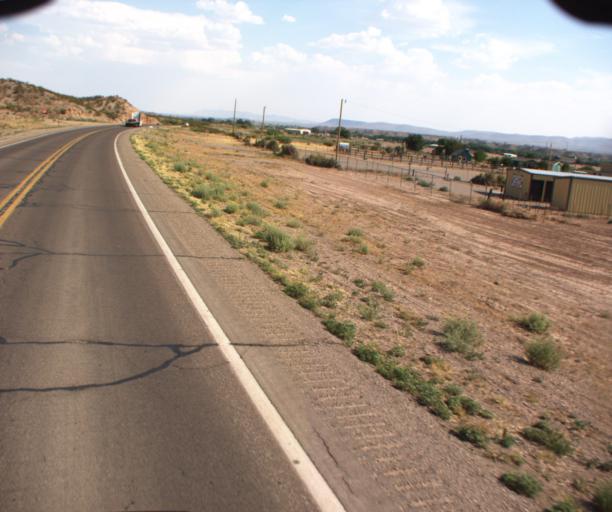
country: US
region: Arizona
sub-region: Greenlee County
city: Clifton
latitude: 32.7365
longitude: -109.0929
